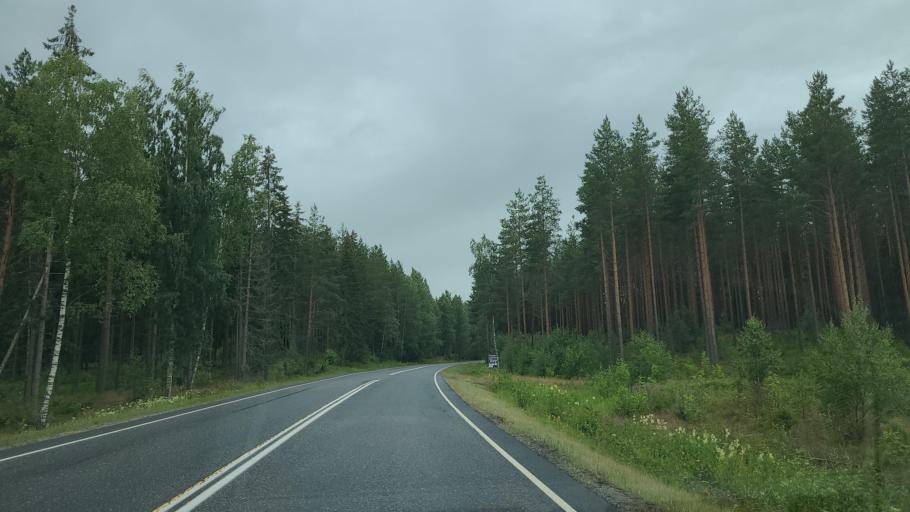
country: FI
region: Varsinais-Suomi
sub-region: Turku
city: Sauvo
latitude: 60.3258
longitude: 22.7138
